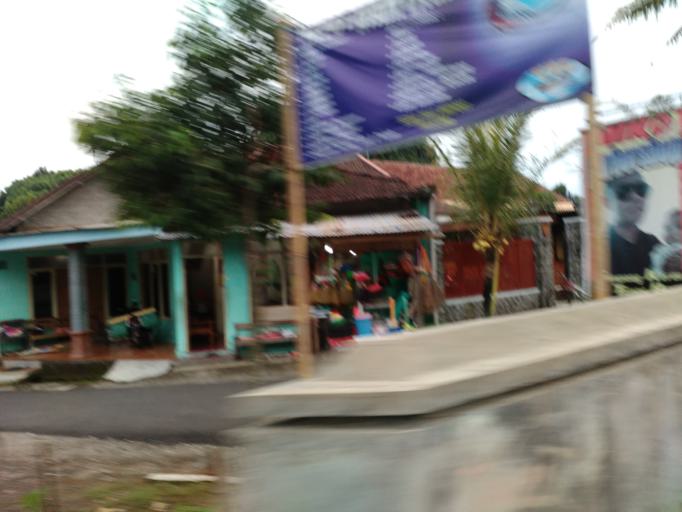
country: ID
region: Central Java
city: Boyolali
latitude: -7.5281
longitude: 110.5936
